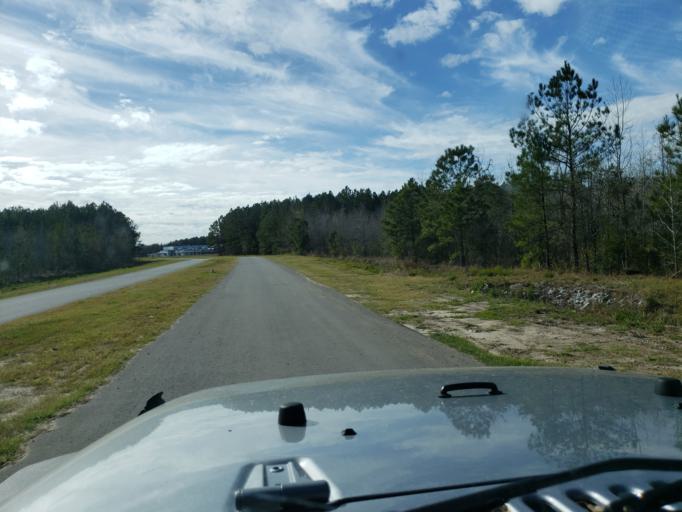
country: US
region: Georgia
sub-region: Chatham County
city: Port Wentworth
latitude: 32.2215
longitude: -81.1903
